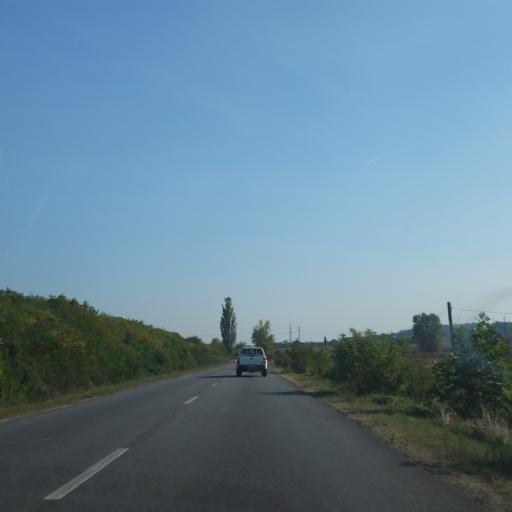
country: RO
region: Arges
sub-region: Comuna Merisani
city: Merisani
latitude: 44.9561
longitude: 24.7579
